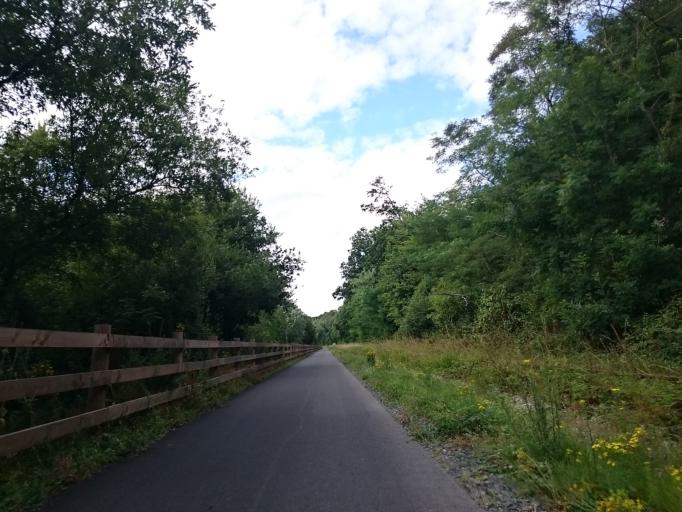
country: FR
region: Lower Normandy
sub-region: Departement du Calvados
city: Thury-Harcourt
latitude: 49.0230
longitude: -0.4650
